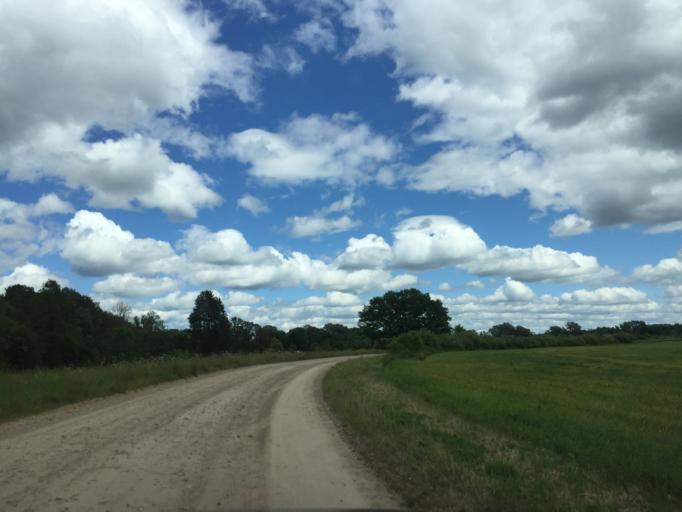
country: LV
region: Lecava
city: Iecava
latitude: 56.5883
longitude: 24.2409
